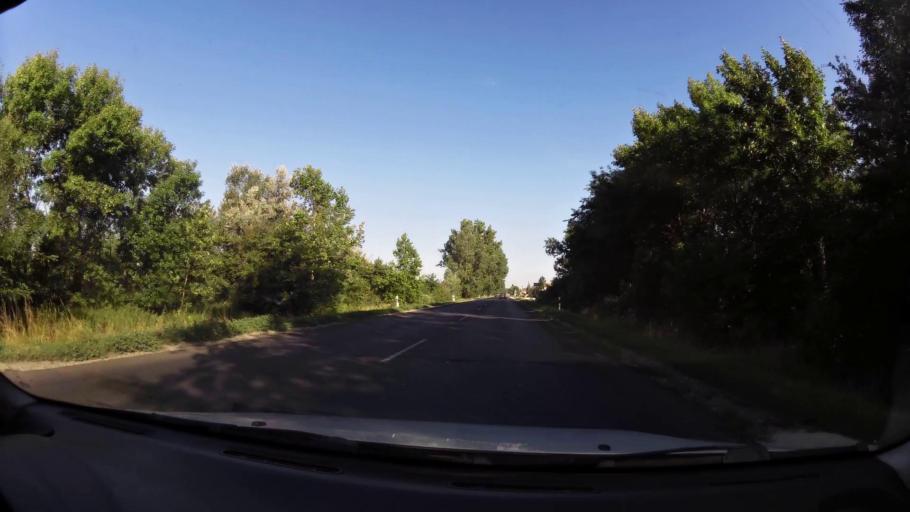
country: HU
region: Pest
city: Monor
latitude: 47.3294
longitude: 19.4522
